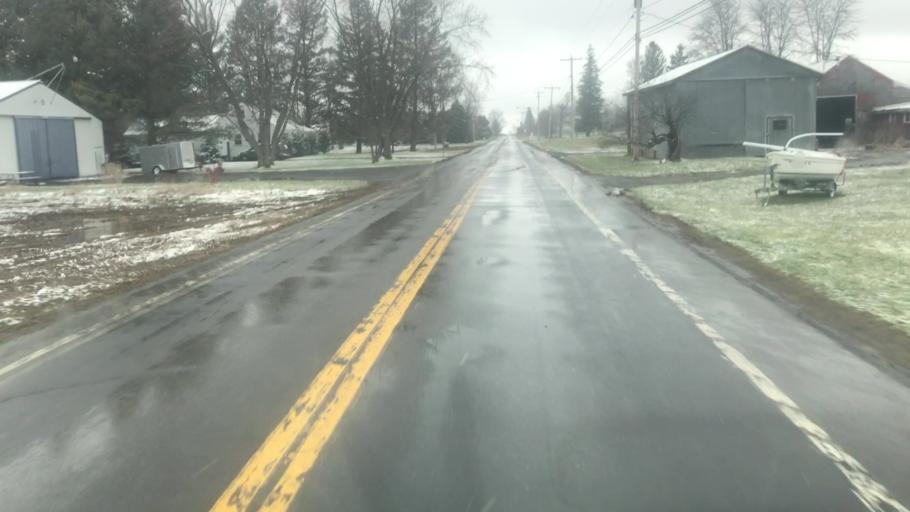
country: US
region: New York
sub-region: Onondaga County
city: Marcellus
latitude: 42.9948
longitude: -76.3911
